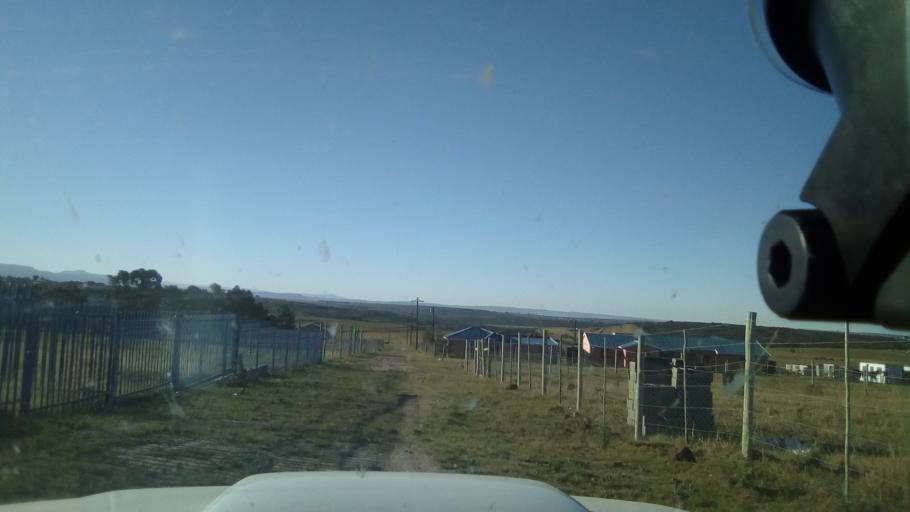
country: ZA
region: Eastern Cape
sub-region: Buffalo City Metropolitan Municipality
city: Bhisho
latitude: -32.9542
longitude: 27.2958
